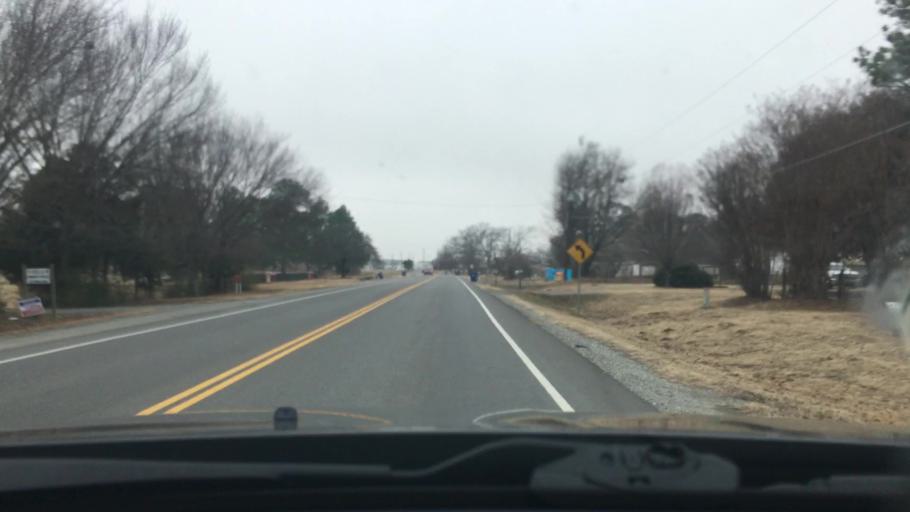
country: US
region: Oklahoma
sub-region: Atoka County
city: Atoka
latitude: 34.3943
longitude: -96.1345
